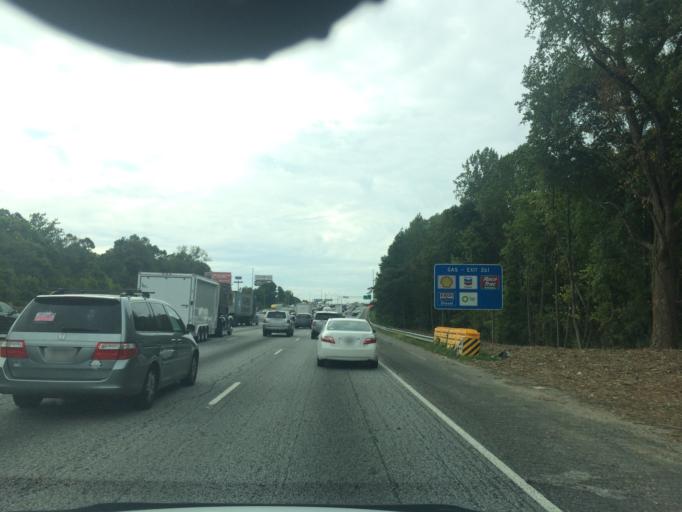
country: US
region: Georgia
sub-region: Cobb County
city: Smyrna
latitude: 33.9300
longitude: -84.4898
